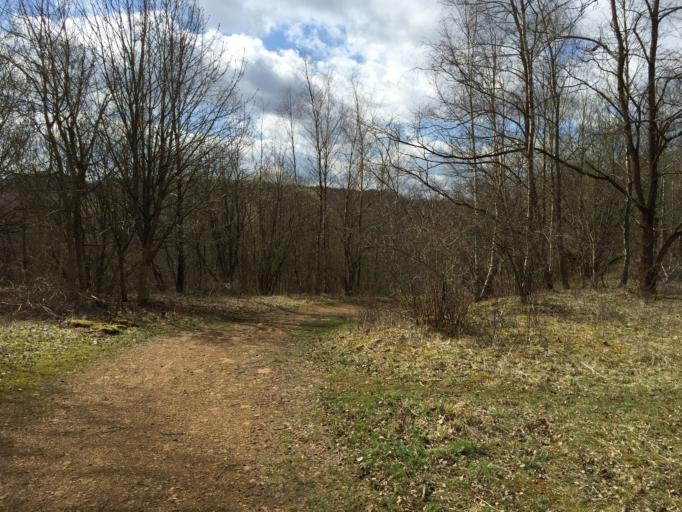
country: LU
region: Luxembourg
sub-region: Canton d'Esch-sur-Alzette
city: Petange
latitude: 49.5424
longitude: 5.8757
